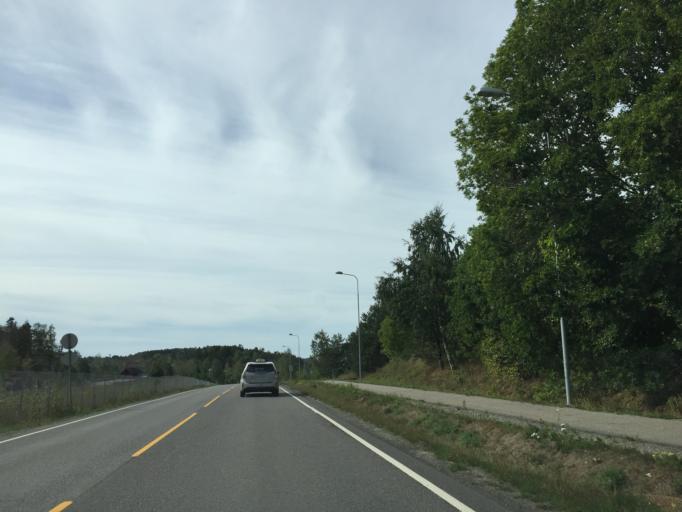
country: NO
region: Ostfold
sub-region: Moss
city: Moss
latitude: 59.4810
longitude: 10.6947
